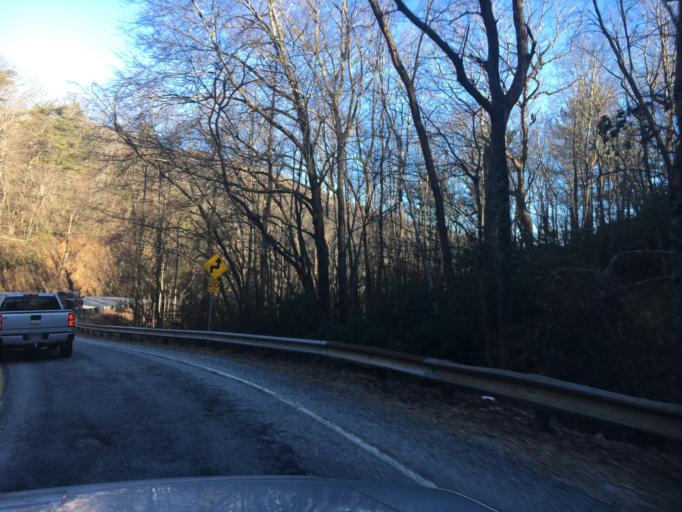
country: US
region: Georgia
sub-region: Union County
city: Blairsville
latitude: 34.7308
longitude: -83.9231
